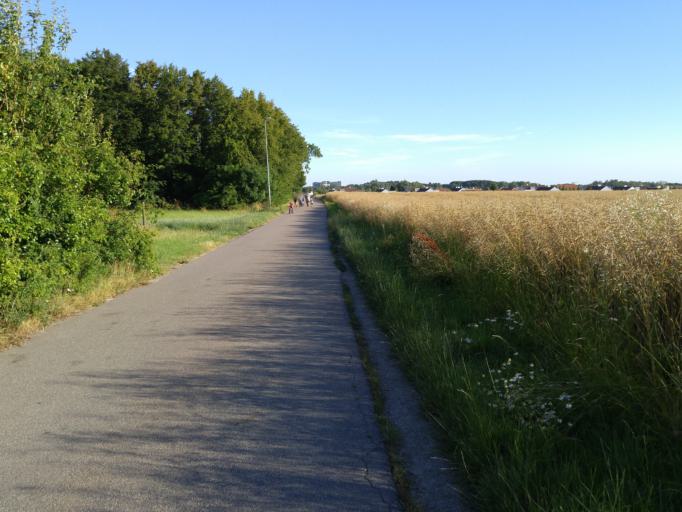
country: SE
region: Skane
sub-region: Lunds Kommun
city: Lund
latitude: 55.7351
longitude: 13.1933
